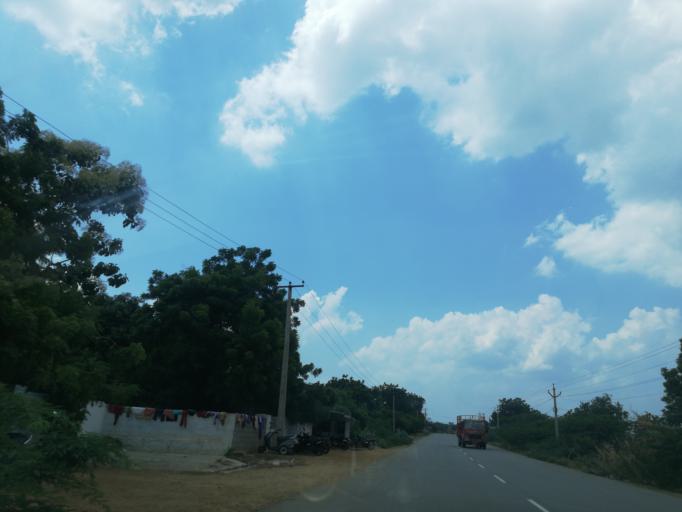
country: IN
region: Andhra Pradesh
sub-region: Guntur
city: Macherla
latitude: 16.5899
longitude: 79.3185
